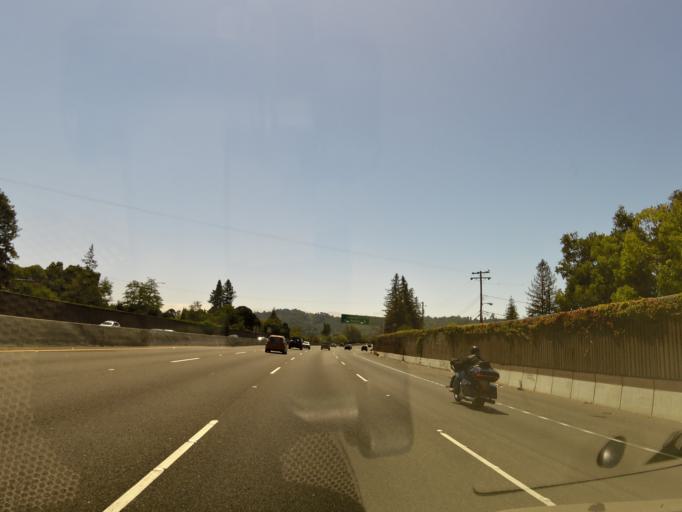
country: US
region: California
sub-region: Marin County
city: San Rafael
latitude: 37.9781
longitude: -122.5208
